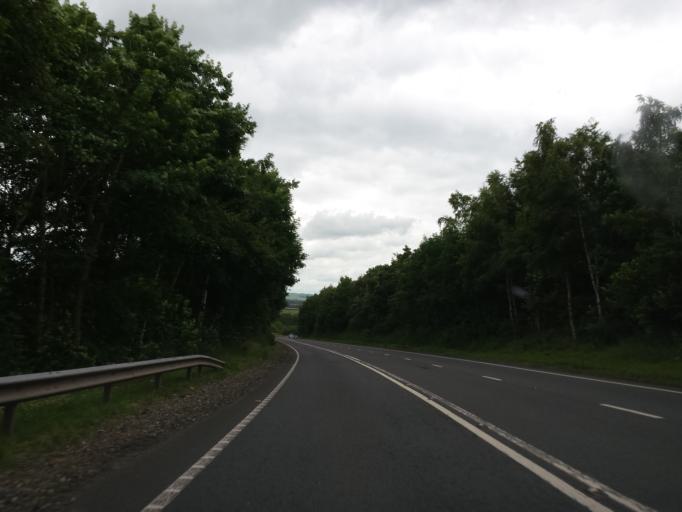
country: GB
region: Scotland
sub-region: Dumfries and Galloway
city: Dumfries
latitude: 55.0597
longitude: -3.6759
